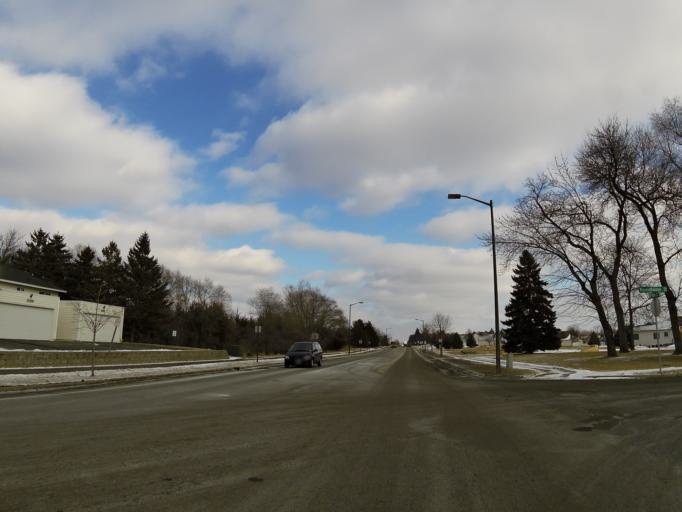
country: US
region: Minnesota
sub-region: Scott County
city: Shakopee
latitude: 44.7974
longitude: -93.5060
